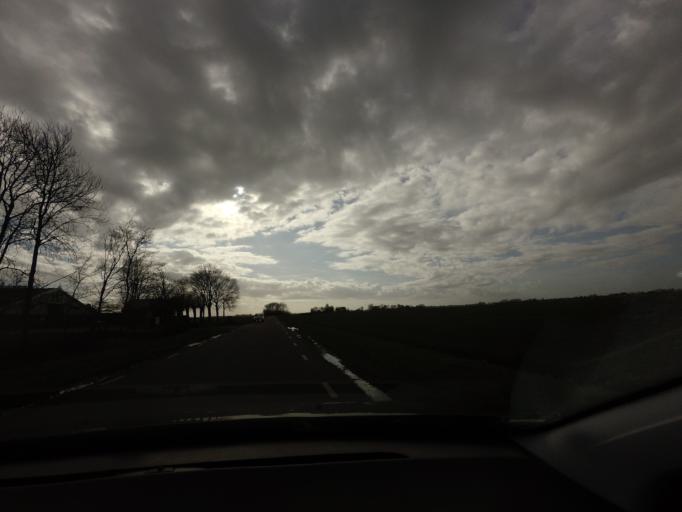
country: NL
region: Friesland
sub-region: Gemeente Boarnsterhim
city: Jirnsum
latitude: 53.0702
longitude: 5.7648
